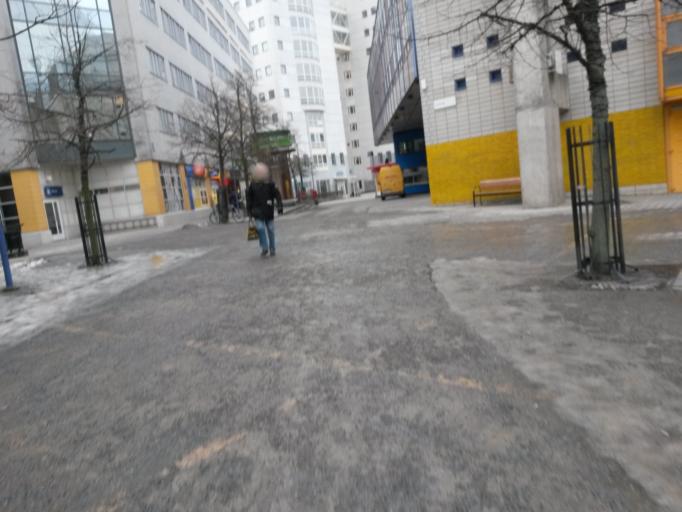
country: SE
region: Stockholm
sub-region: Stockholms Kommun
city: Arsta
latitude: 59.2935
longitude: 18.0818
